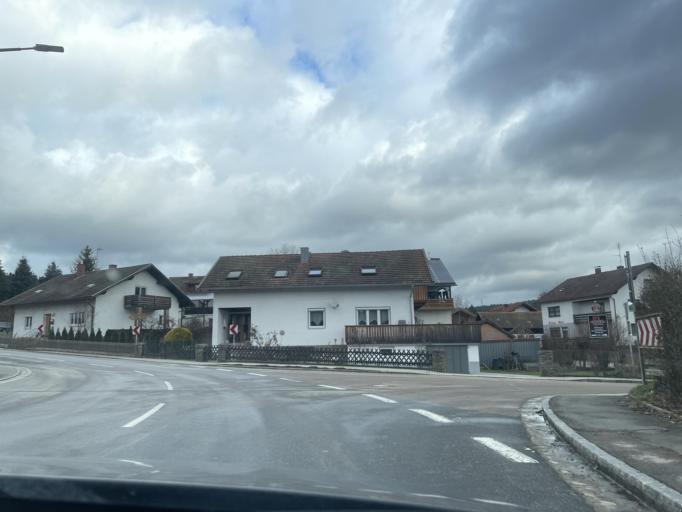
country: DE
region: Bavaria
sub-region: Upper Palatinate
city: Blaibach
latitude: 49.1684
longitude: 12.8060
